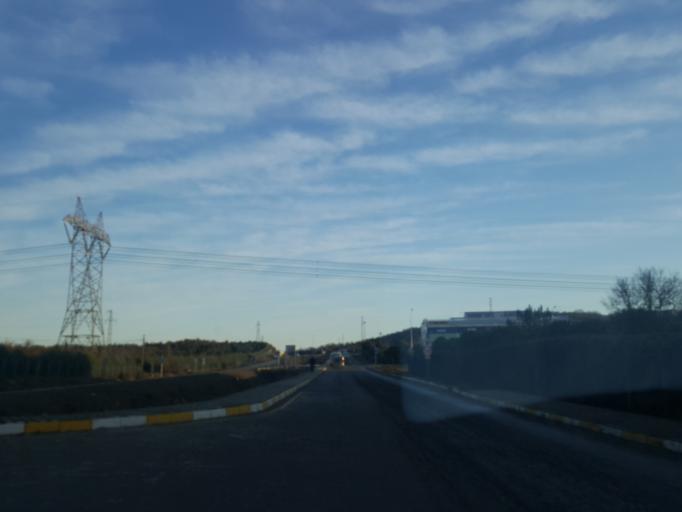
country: TR
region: Kocaeli
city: Tavsanli
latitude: 40.8609
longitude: 29.5584
